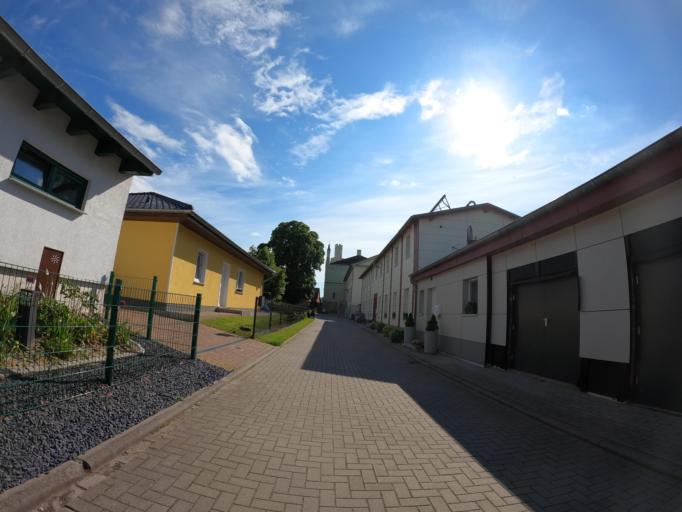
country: DE
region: Mecklenburg-Vorpommern
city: Kramerhof
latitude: 54.3391
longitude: 13.0363
